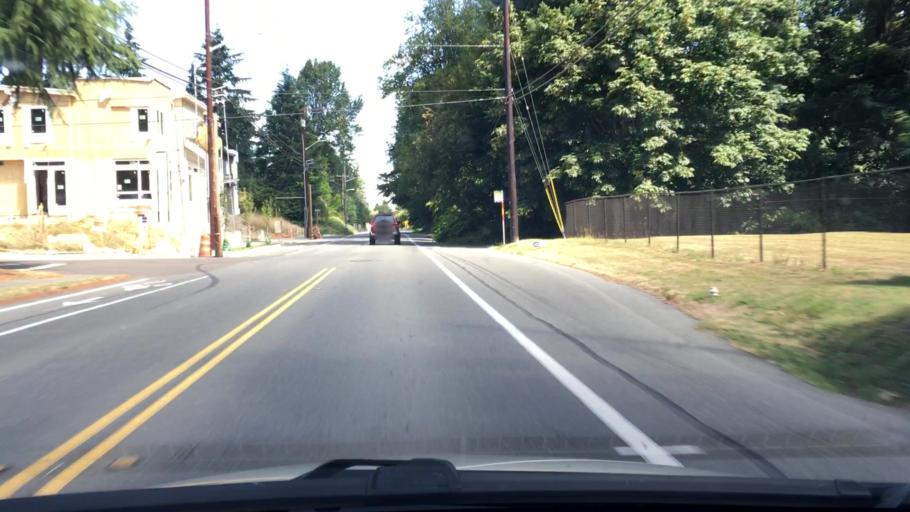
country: US
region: Washington
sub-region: King County
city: Kingsgate
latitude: 47.7010
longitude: -122.1646
